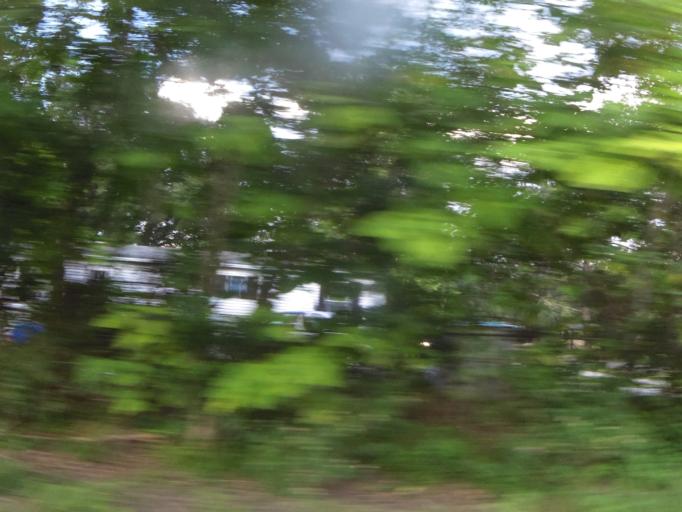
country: US
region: Florida
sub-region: Duval County
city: Jacksonville
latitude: 30.3311
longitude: -81.7839
